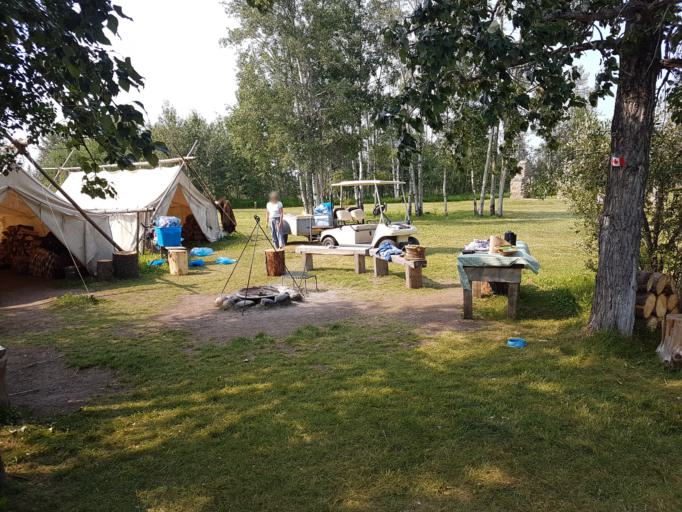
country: CA
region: Alberta
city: Rocky Mountain House
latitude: 52.3616
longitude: -114.9690
